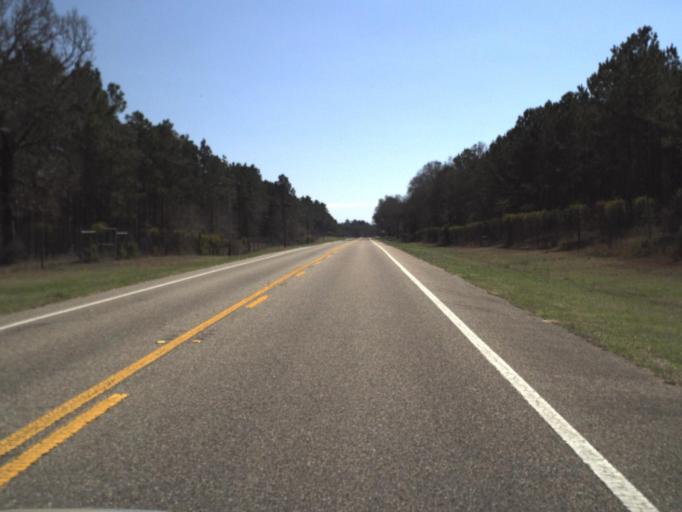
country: US
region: Florida
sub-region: Jackson County
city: Sneads
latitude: 30.5960
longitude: -85.0281
